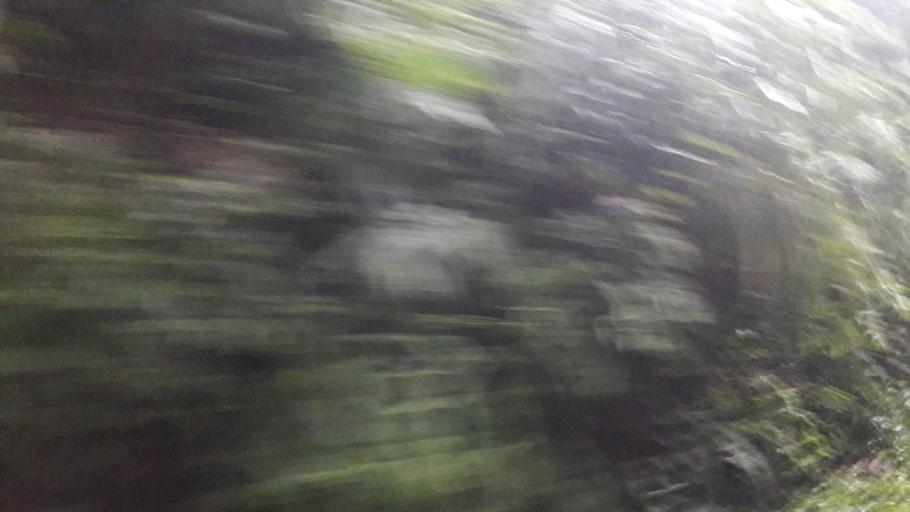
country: ID
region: West Java
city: Cipeundeuy
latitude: -6.6531
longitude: 106.5198
